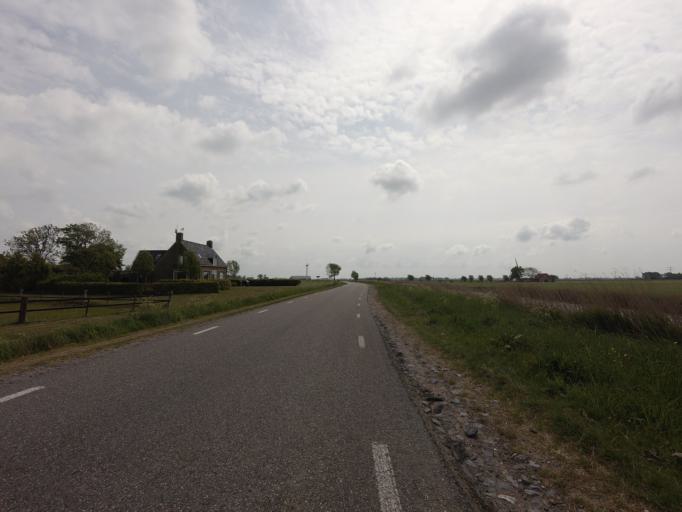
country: NL
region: Friesland
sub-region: Sudwest Fryslan
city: Bolsward
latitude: 53.1042
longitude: 5.5122
